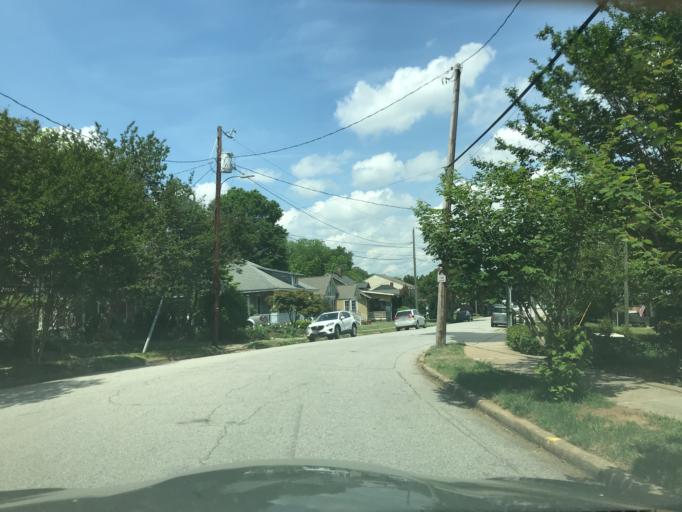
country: US
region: North Carolina
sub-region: Wake County
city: Raleigh
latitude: 35.7905
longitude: -78.6327
